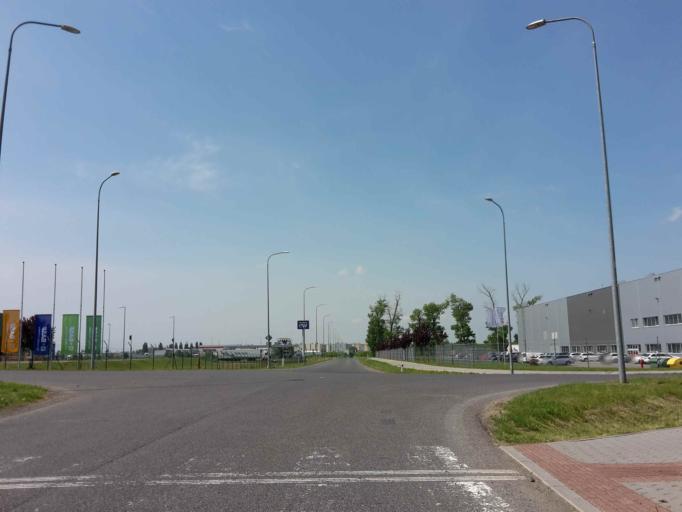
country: SK
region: Bratislavsky
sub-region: Okres Malacky
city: Malacky
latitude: 48.4215
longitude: 17.0361
